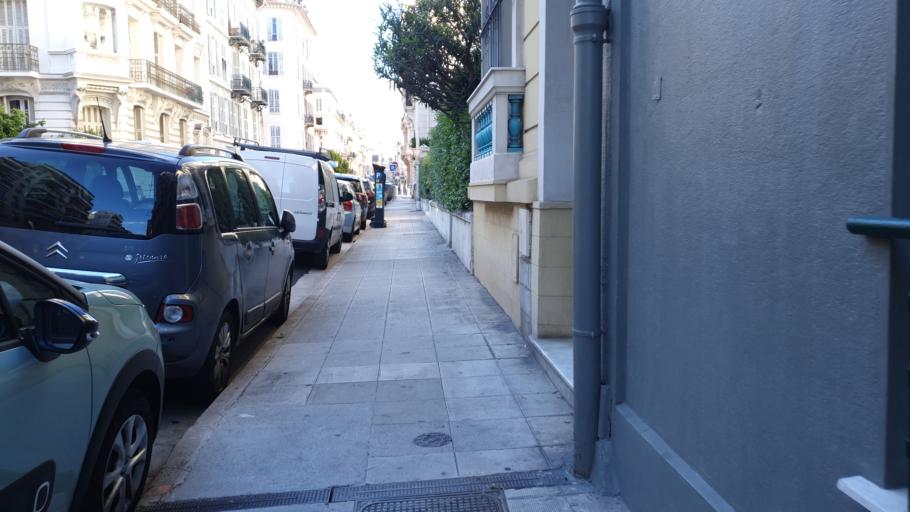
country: FR
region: Provence-Alpes-Cote d'Azur
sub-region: Departement des Alpes-Maritimes
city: Nice
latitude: 43.6998
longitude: 7.2603
